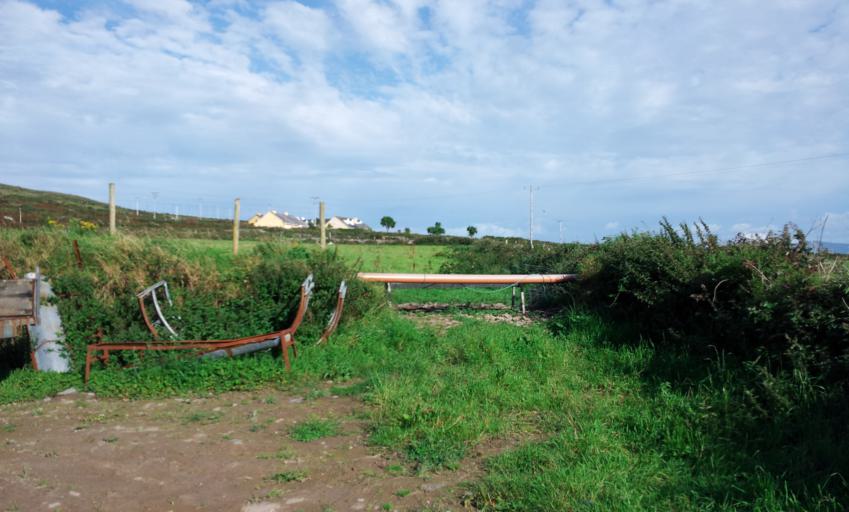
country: IE
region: Munster
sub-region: Ciarrai
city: Dingle
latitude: 52.1347
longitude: -10.3603
